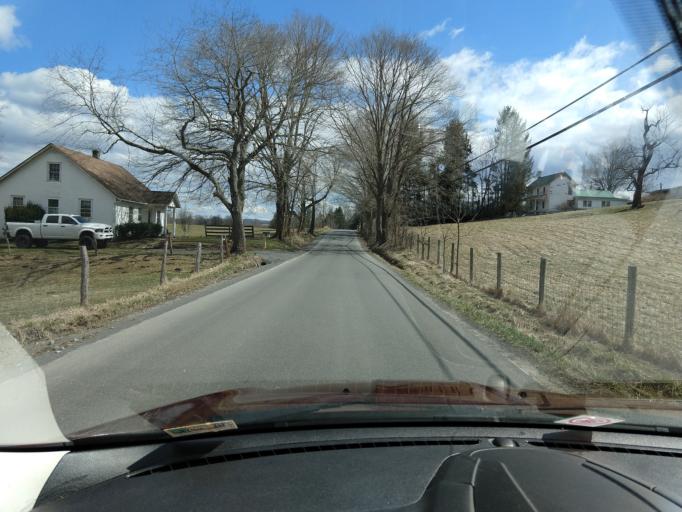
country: US
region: West Virginia
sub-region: Greenbrier County
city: Fairlea
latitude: 37.8111
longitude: -80.5021
